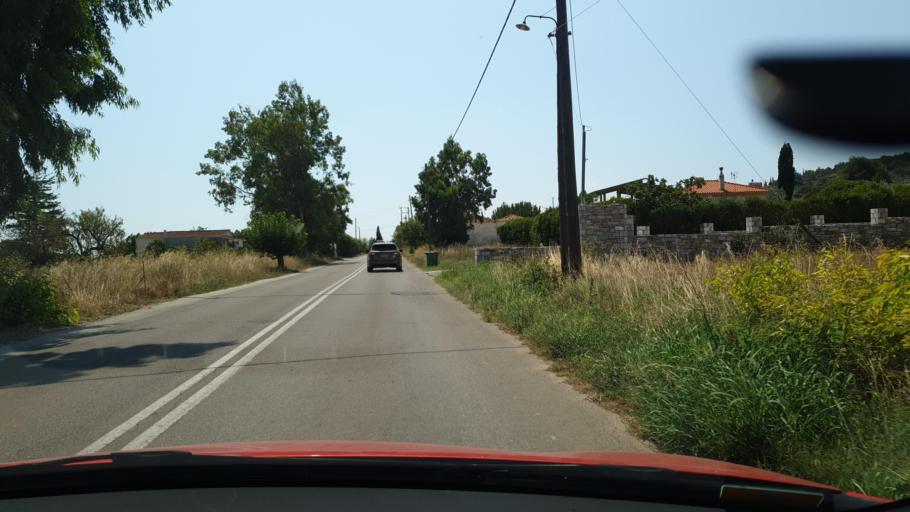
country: GR
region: Central Greece
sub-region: Nomos Evvoias
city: Oxilithos
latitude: 38.4767
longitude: 24.1179
